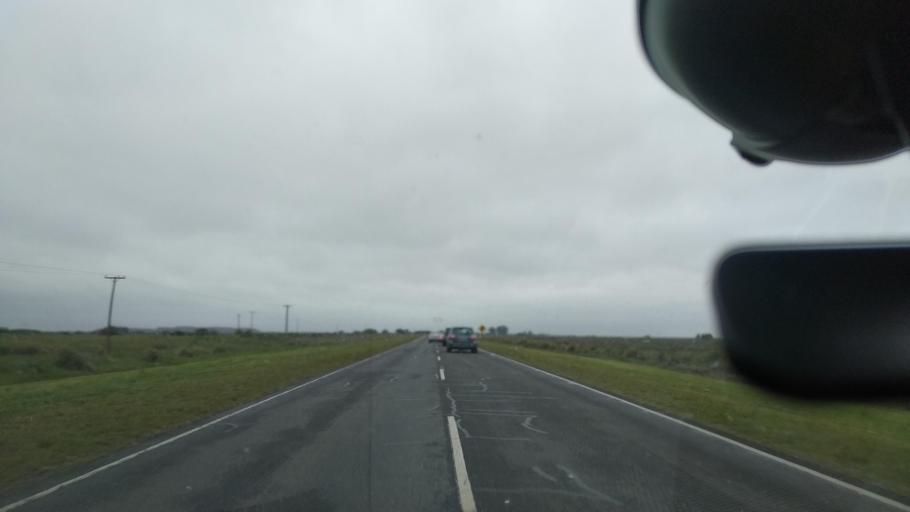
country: AR
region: Buenos Aires
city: Veronica
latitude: -35.6961
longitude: -57.3499
